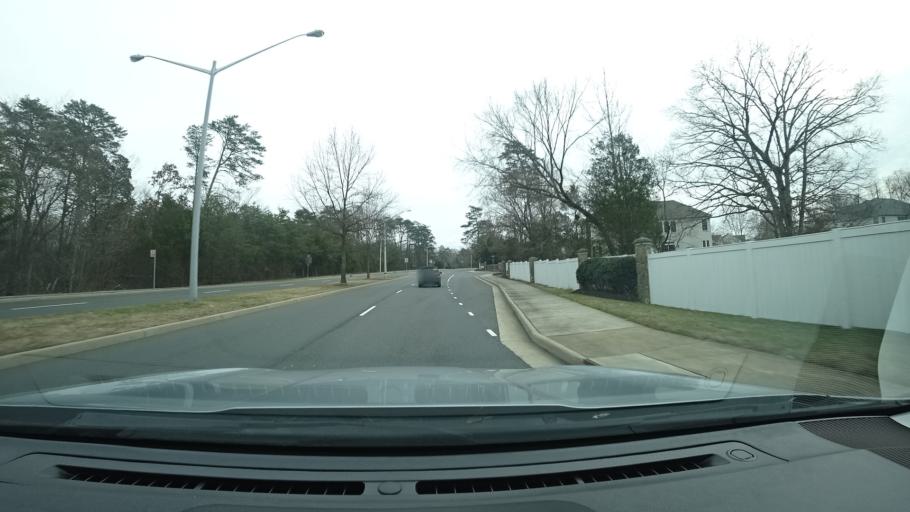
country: US
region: Virginia
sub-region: Fairfax County
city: Herndon
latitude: 38.9744
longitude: -77.3707
